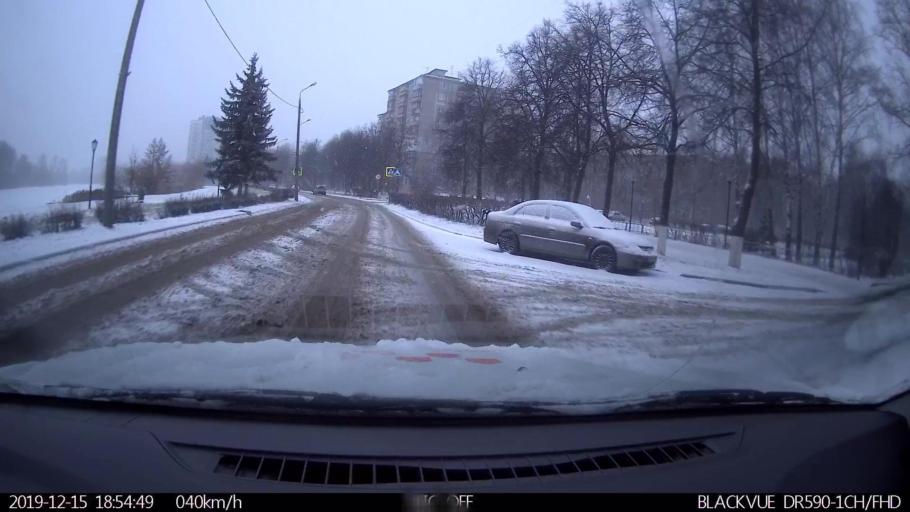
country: RU
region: Nizjnij Novgorod
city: Gorbatovka
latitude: 56.3445
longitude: 43.8501
